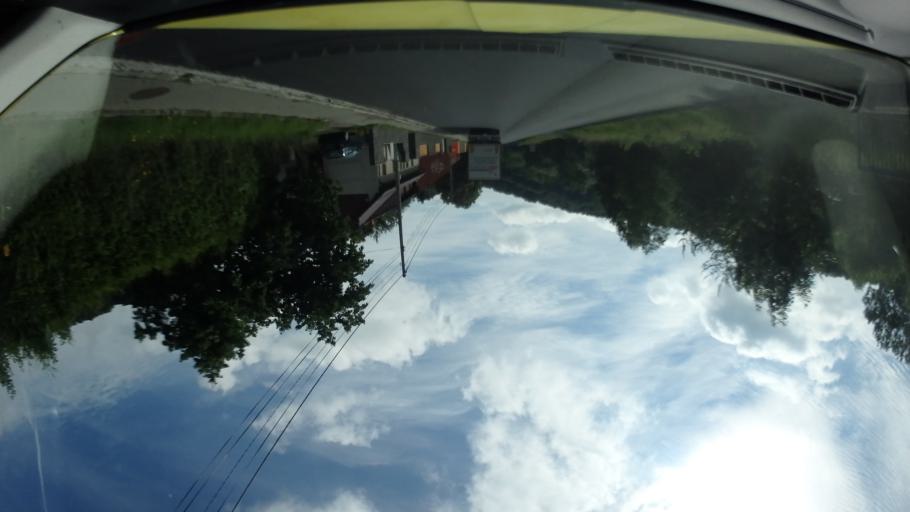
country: CZ
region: Moravskoslezsky
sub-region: Okres Novy Jicin
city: Novy Jicin
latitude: 49.5726
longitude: 18.0225
